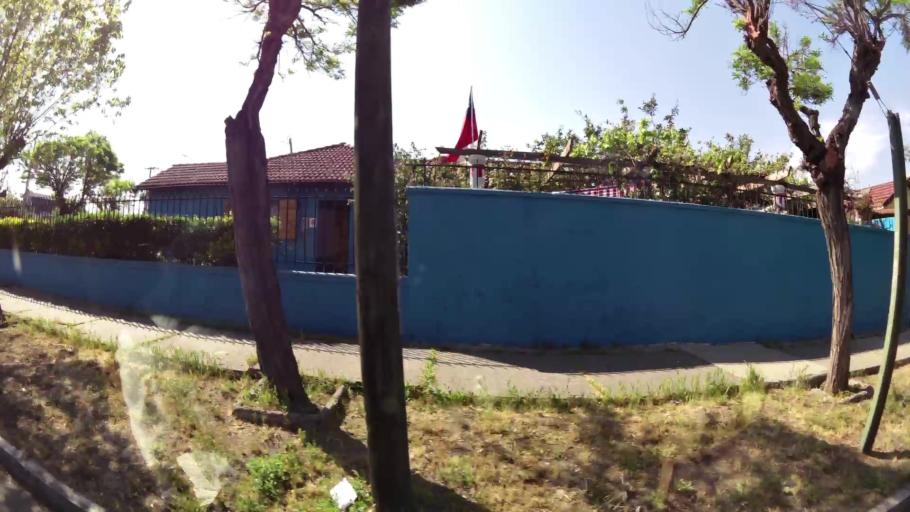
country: CL
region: Santiago Metropolitan
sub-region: Provincia de Maipo
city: San Bernardo
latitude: -33.5867
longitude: -70.6962
